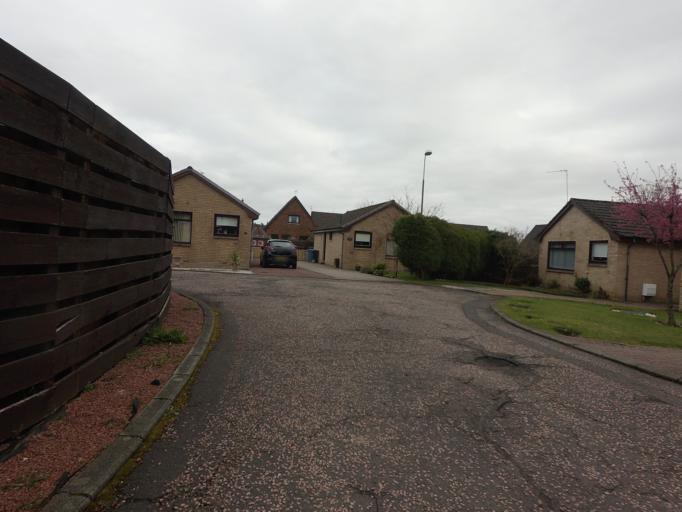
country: GB
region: Scotland
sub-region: West Lothian
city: Livingston
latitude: 55.8885
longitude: -3.5386
